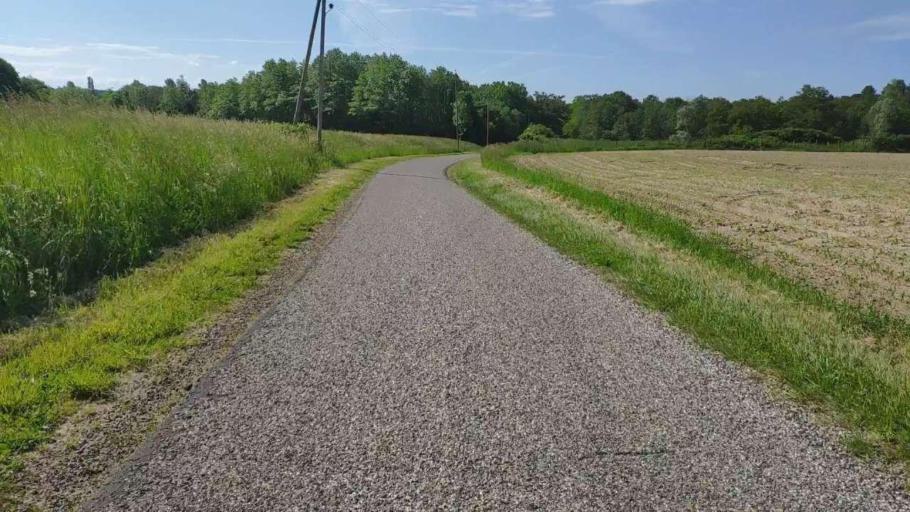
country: FR
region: Franche-Comte
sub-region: Departement du Jura
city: Bletterans
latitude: 46.7030
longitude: 5.4704
